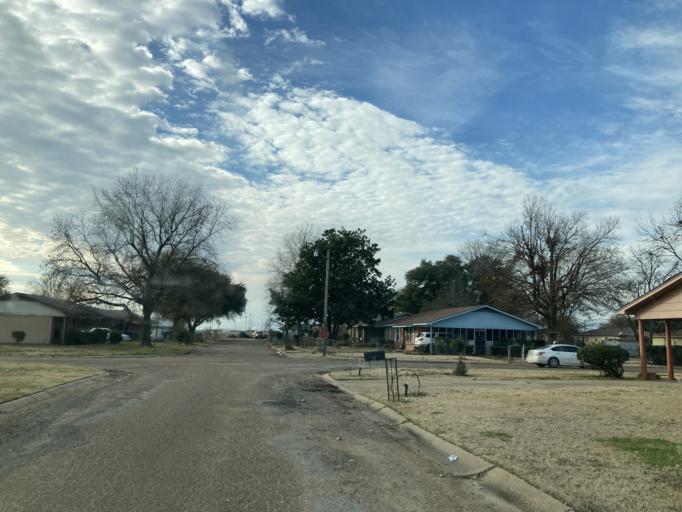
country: US
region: Mississippi
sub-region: Humphreys County
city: Belzoni
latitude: 33.1694
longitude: -90.5019
